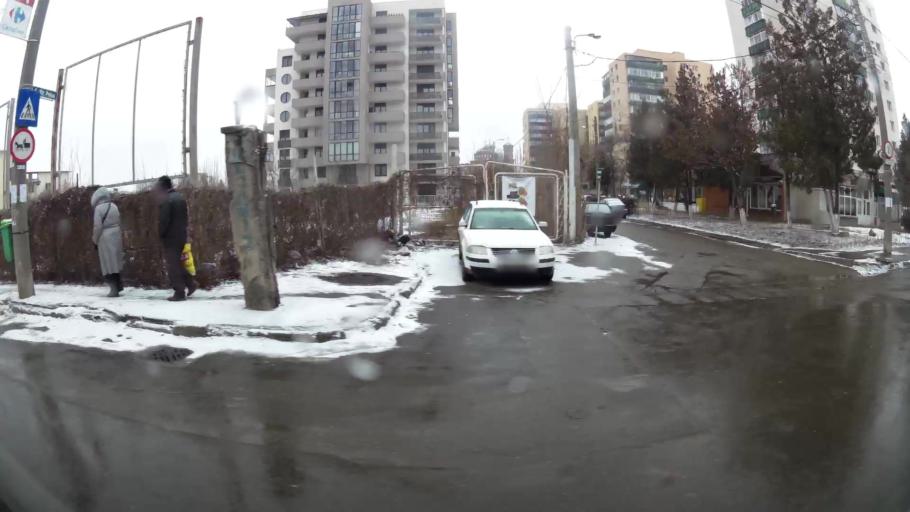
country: RO
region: Prahova
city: Ploiesti
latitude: 44.9576
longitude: 26.0129
